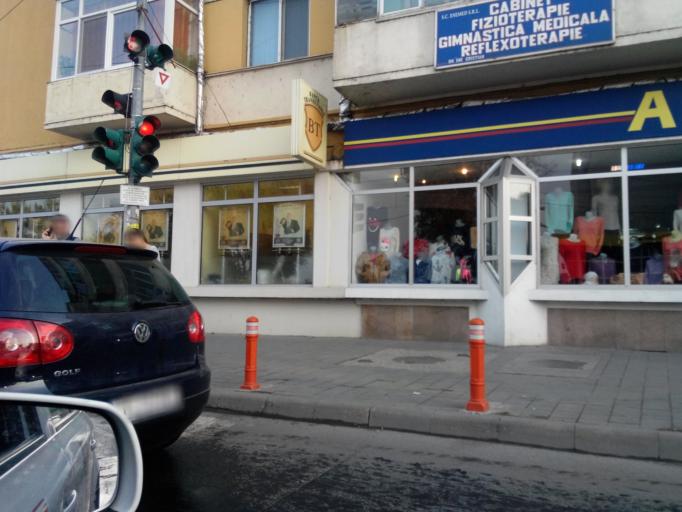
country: RO
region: Tulcea
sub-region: Municipiul Tulcea
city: Tulcea
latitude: 45.1788
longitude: 28.8022
